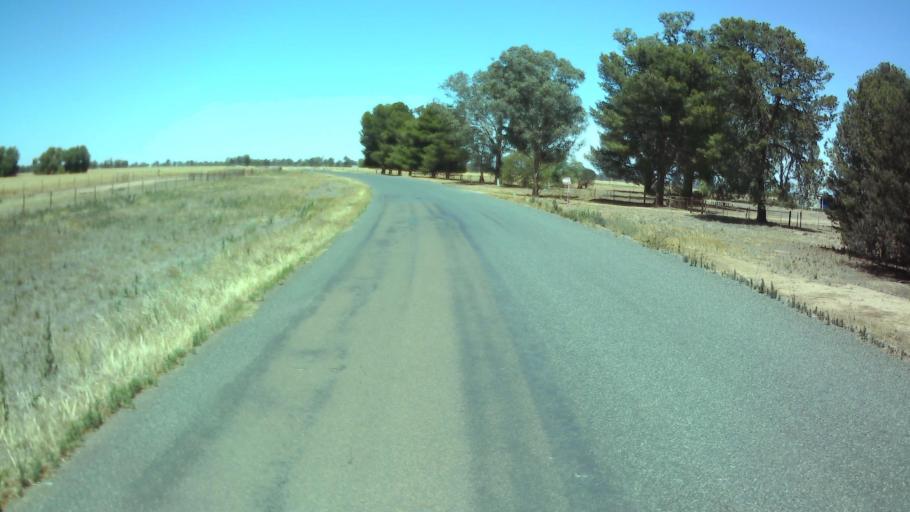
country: AU
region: New South Wales
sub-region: Weddin
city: Grenfell
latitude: -34.0465
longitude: 147.7828
